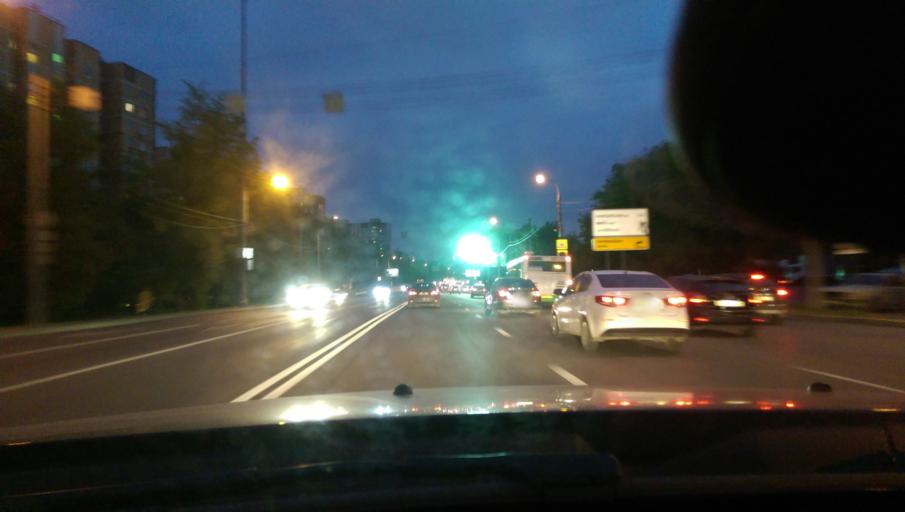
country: RU
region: Moscow
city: Vatutino
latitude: 55.8927
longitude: 37.6737
